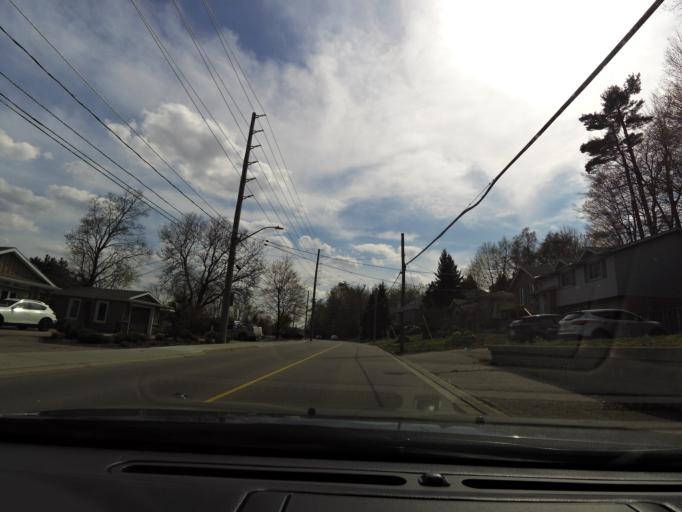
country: CA
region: Ontario
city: Cambridge
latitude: 43.3937
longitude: -80.3743
